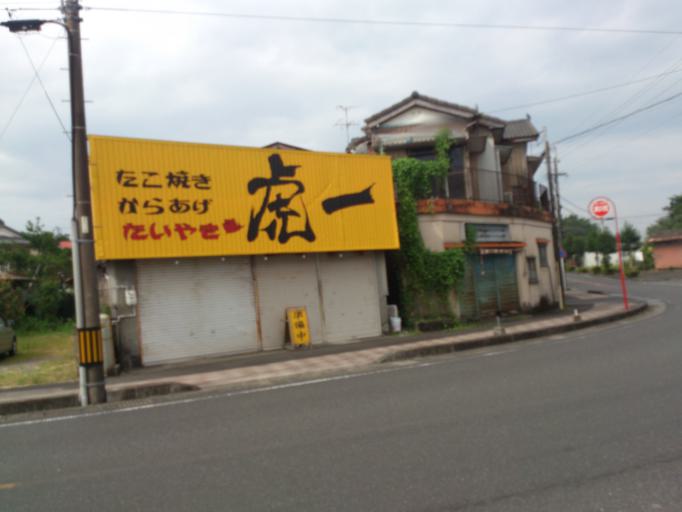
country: JP
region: Kagoshima
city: Kanoya
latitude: 31.3501
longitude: 130.9410
